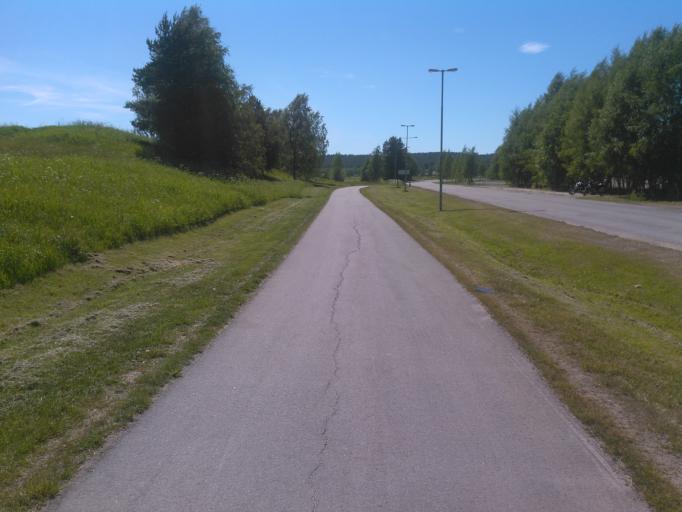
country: SE
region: Vaesterbotten
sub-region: Umea Kommun
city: Roback
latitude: 63.8199
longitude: 20.2040
